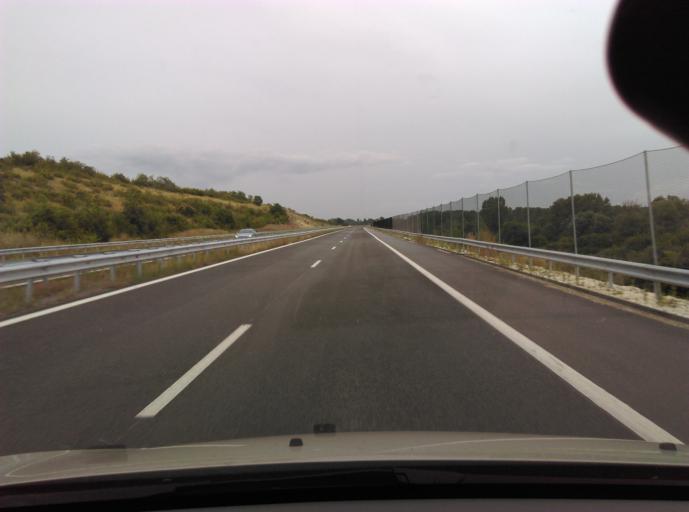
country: BG
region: Stara Zagora
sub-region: Obshtina Chirpan
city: Chirpan
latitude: 42.0959
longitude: 25.4373
